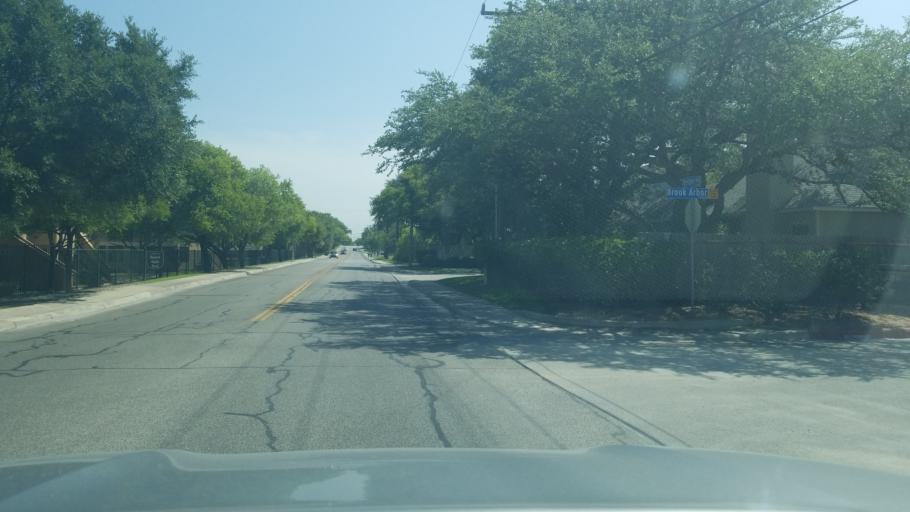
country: US
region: Texas
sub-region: Bexar County
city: Hollywood Park
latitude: 29.5683
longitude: -98.4753
